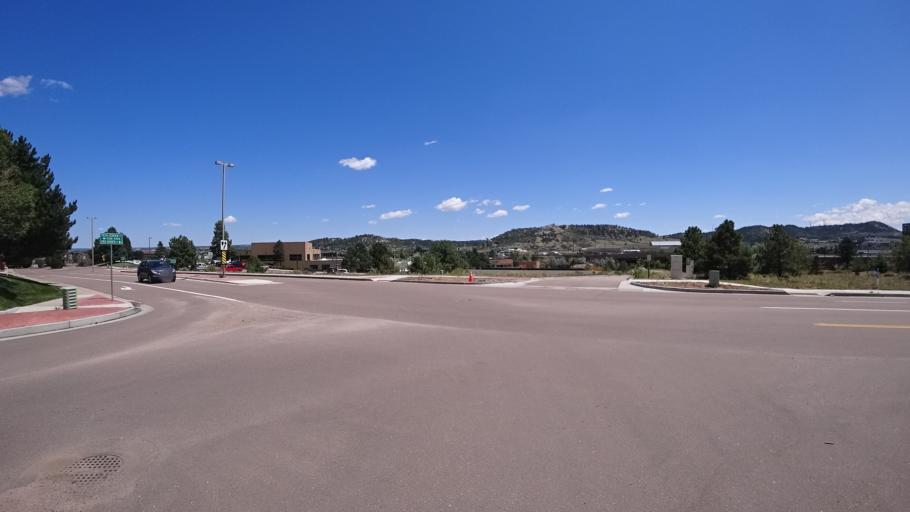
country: US
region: Colorado
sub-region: El Paso County
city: Colorado Springs
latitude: 38.9116
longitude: -104.8258
